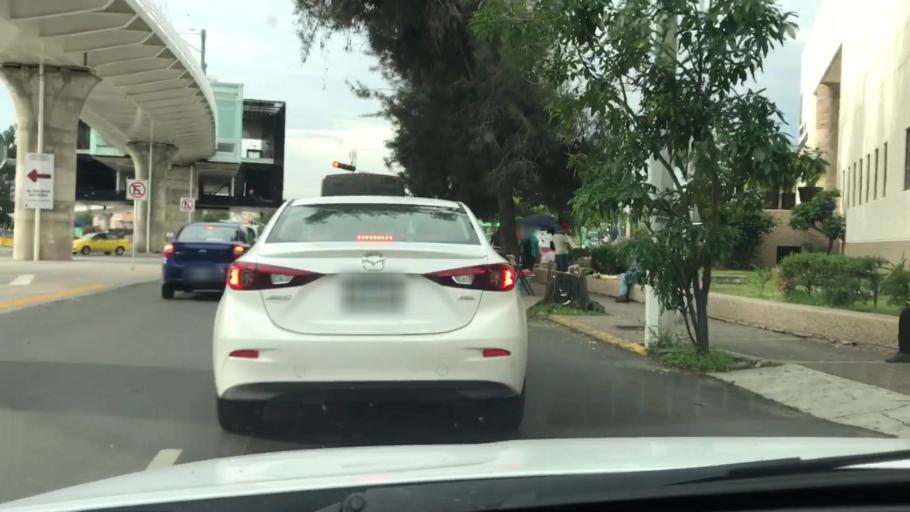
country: MX
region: Jalisco
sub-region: Zapopan
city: Zapopan
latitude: 20.7217
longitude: -103.3876
